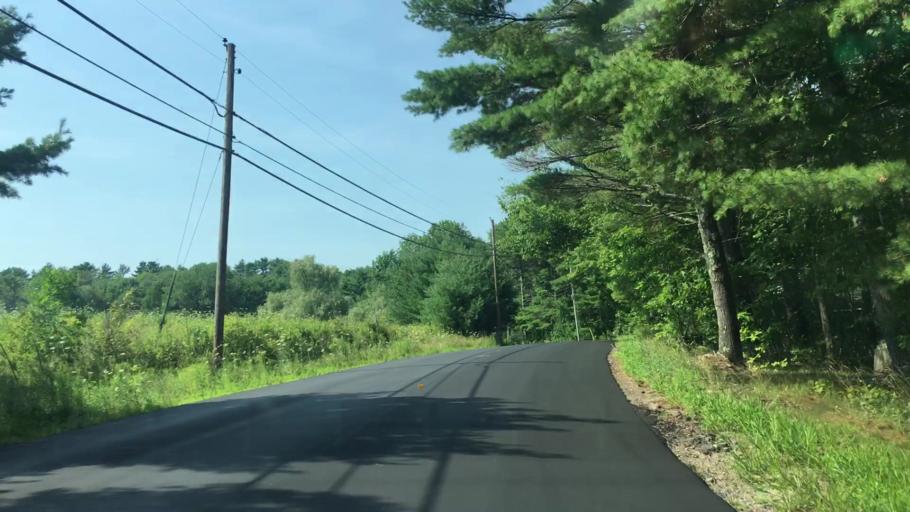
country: US
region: Maine
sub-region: Sagadahoc County
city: North Bath
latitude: 43.9441
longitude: -69.8008
